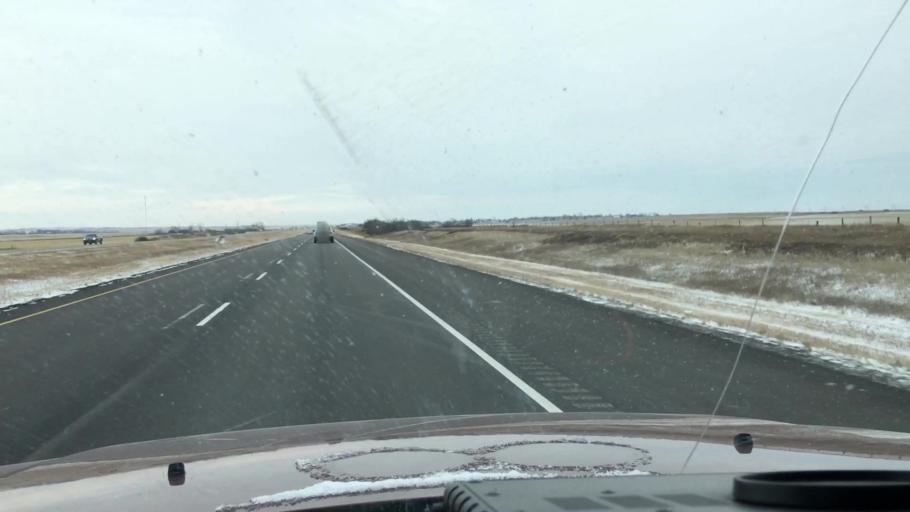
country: CA
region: Saskatchewan
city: Saskatoon
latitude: 51.8363
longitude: -106.5035
